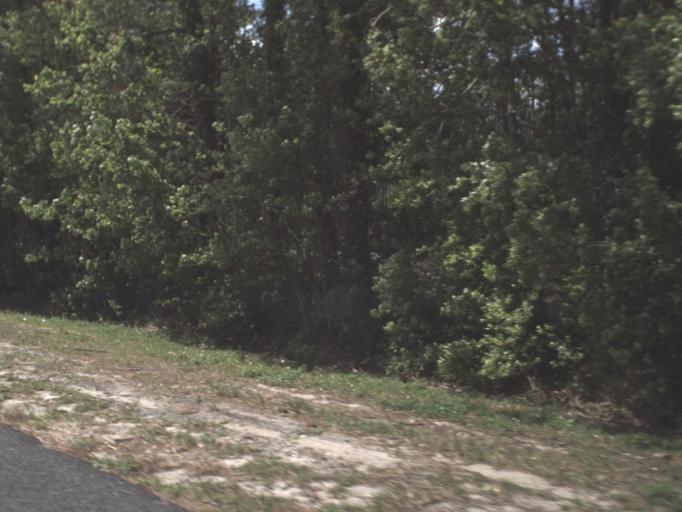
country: US
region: Florida
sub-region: Flagler County
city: Bunnell
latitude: 29.4003
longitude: -81.1942
